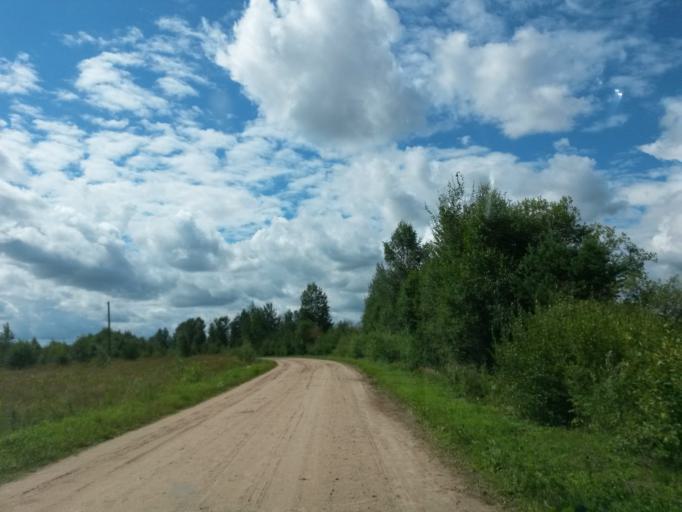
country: RU
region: Jaroslavl
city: Tutayev
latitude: 57.9469
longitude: 39.4537
